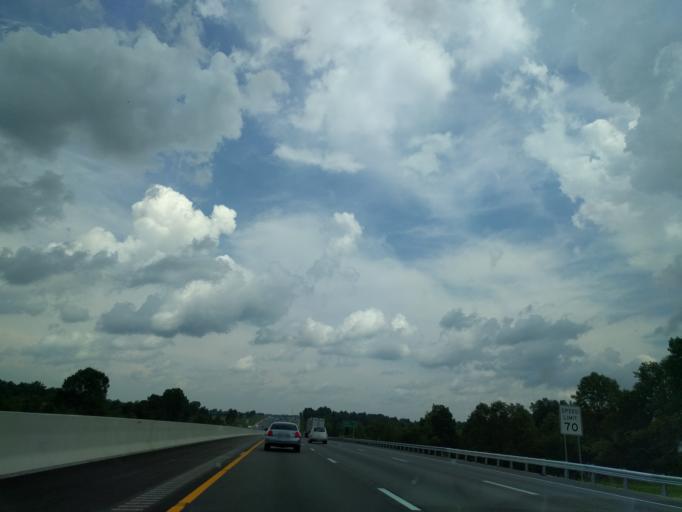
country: US
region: Kentucky
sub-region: Larue County
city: Hodgenville
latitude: 37.4725
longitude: -85.8818
